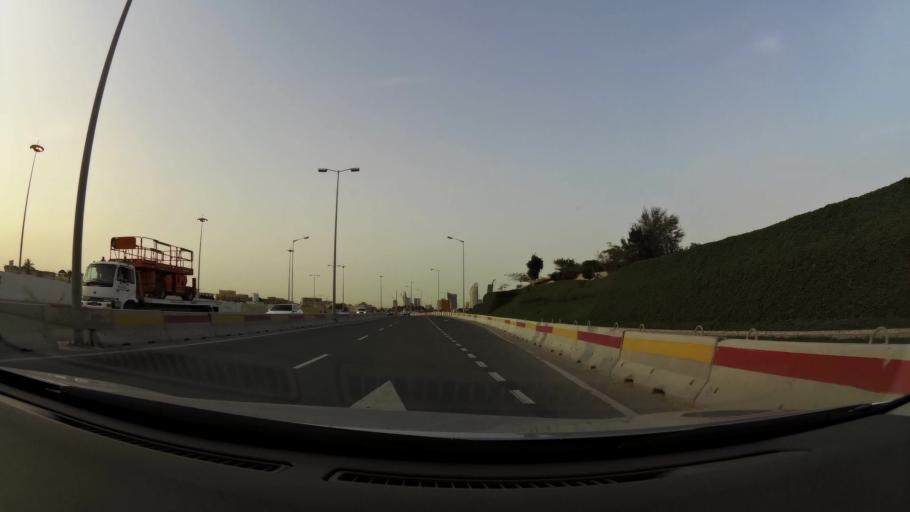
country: QA
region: Baladiyat ad Dawhah
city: Doha
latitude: 25.3581
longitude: 51.5210
